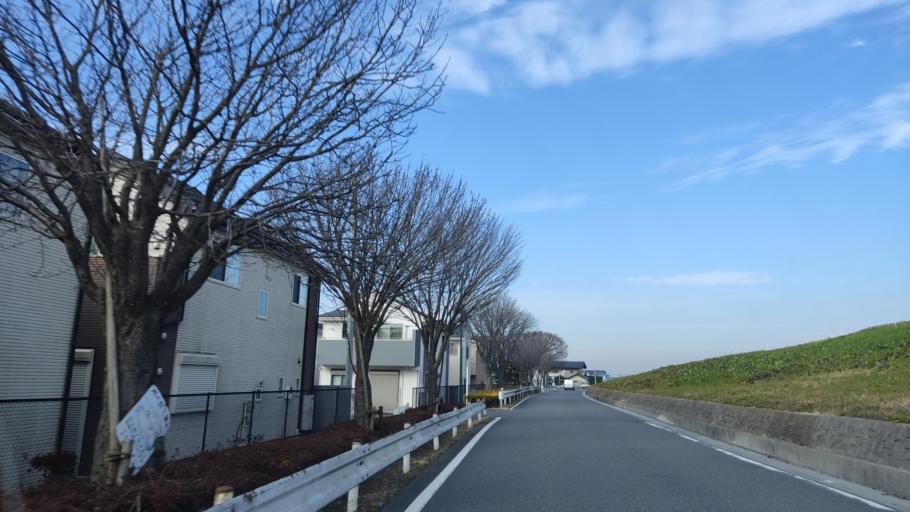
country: JP
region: Chiba
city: Nagareyama
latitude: 35.8215
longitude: 139.8864
